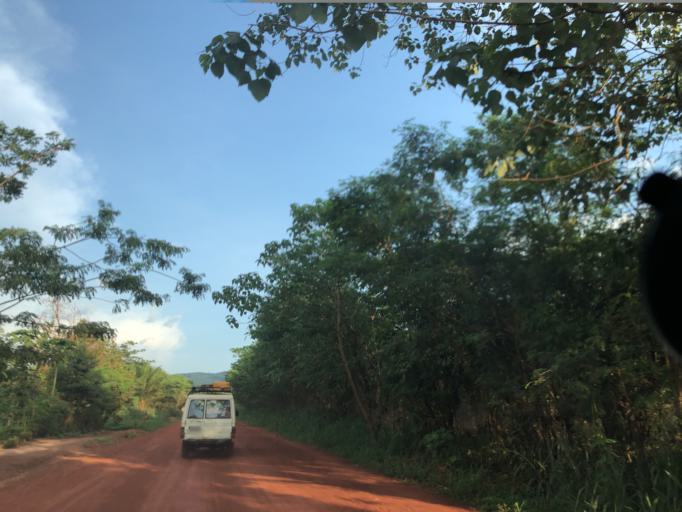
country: CF
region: Bangui
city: Bangui
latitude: 4.3192
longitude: 18.6073
